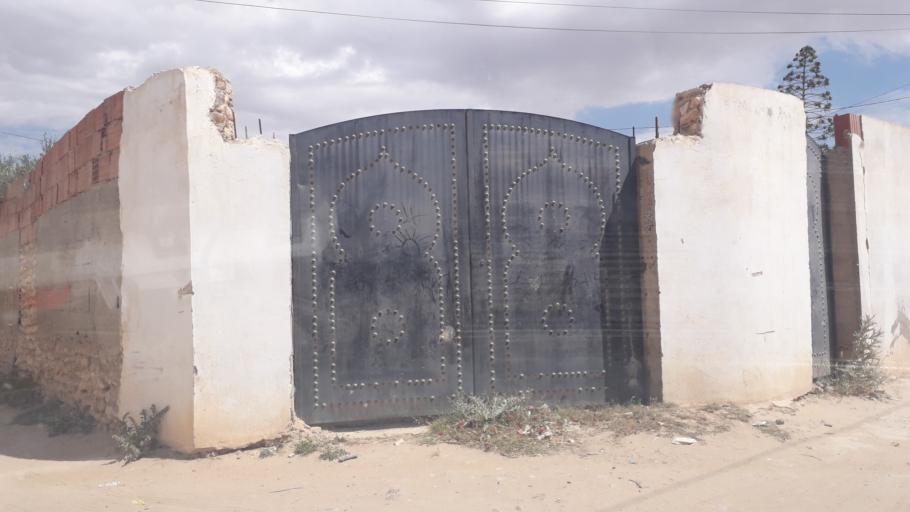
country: TN
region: Safaqis
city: Al Qarmadah
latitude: 34.8421
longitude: 10.7755
